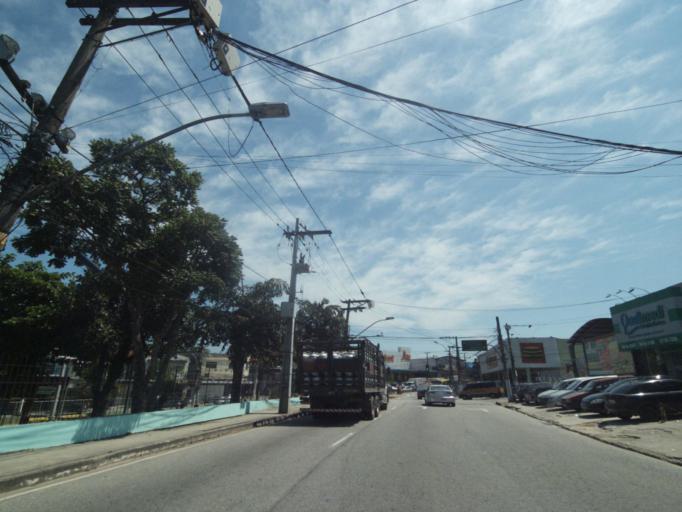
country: BR
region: Rio de Janeiro
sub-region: Niteroi
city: Niteroi
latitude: -22.9064
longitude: -43.0661
